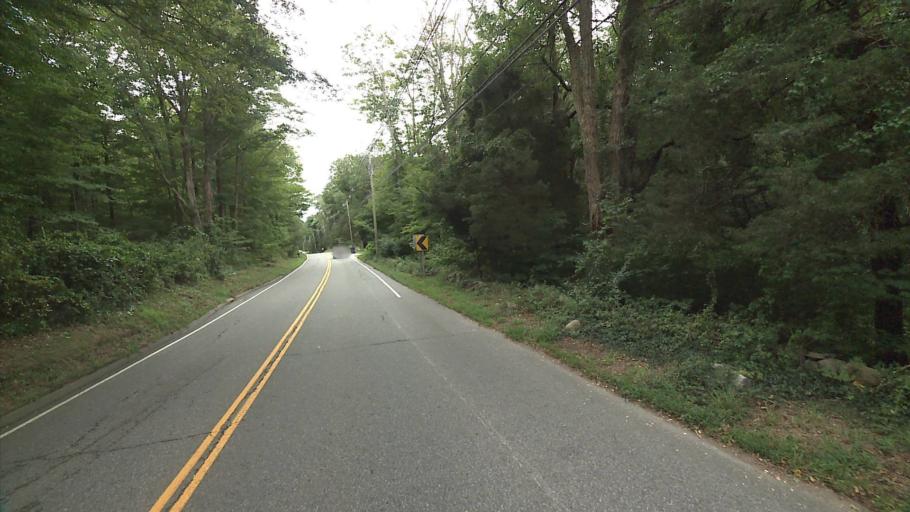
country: US
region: Connecticut
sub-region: Middlesex County
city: Essex Village
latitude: 41.3425
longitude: -72.3398
